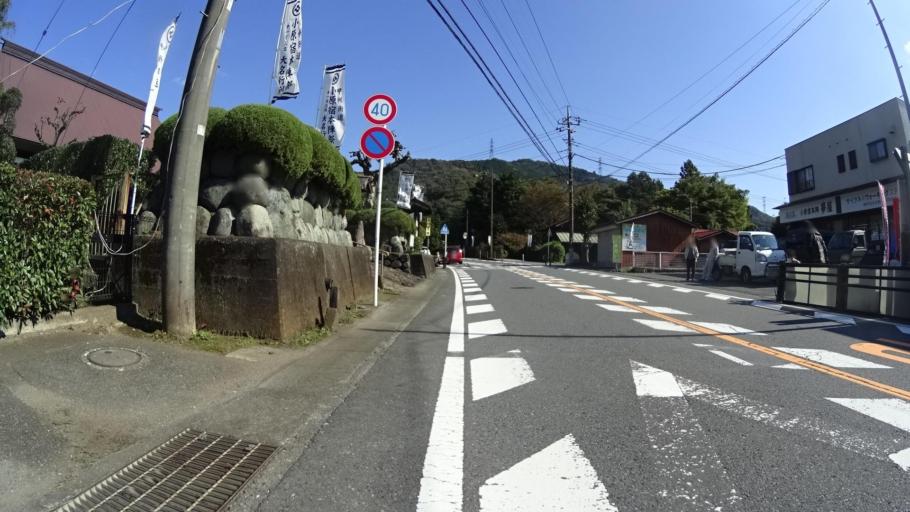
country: JP
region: Yamanashi
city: Uenohara
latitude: 35.6212
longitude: 139.1999
